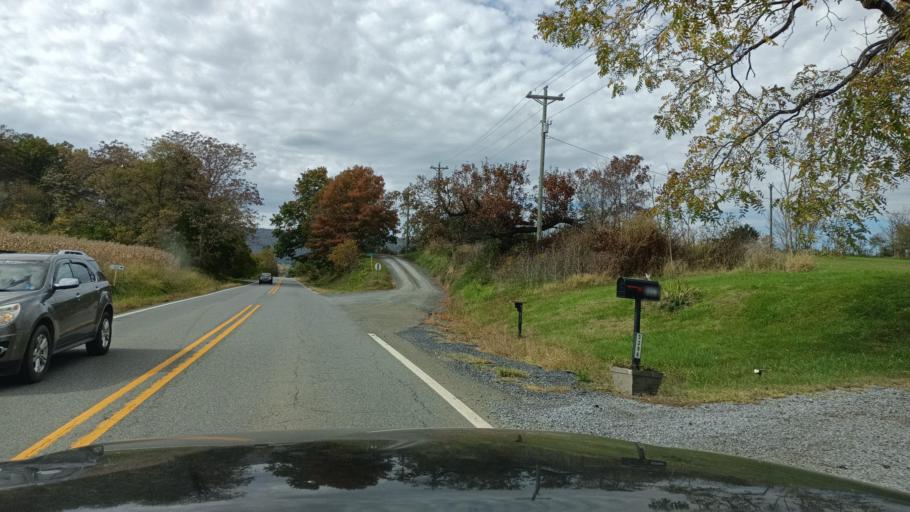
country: US
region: Virginia
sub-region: Shenandoah County
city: Strasburg
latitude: 39.0317
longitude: -78.3736
